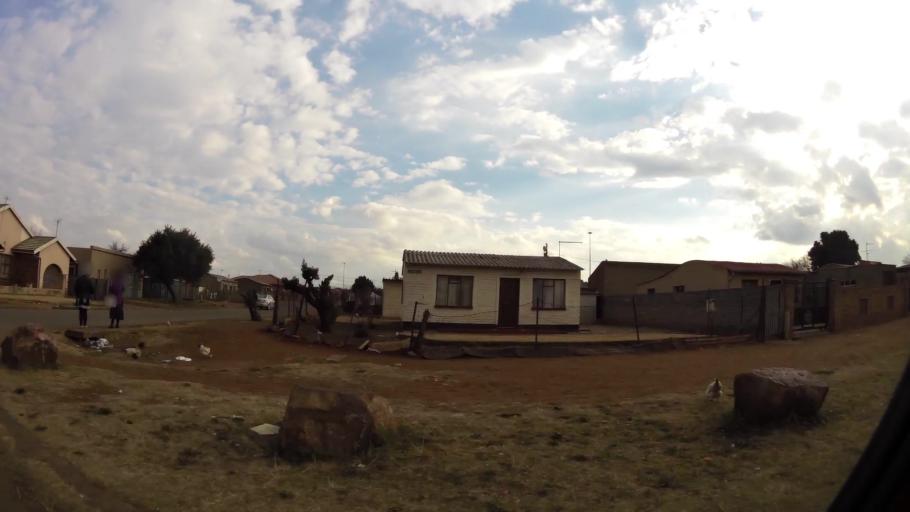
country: ZA
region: Gauteng
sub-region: Sedibeng District Municipality
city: Vereeniging
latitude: -26.6852
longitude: 27.8789
